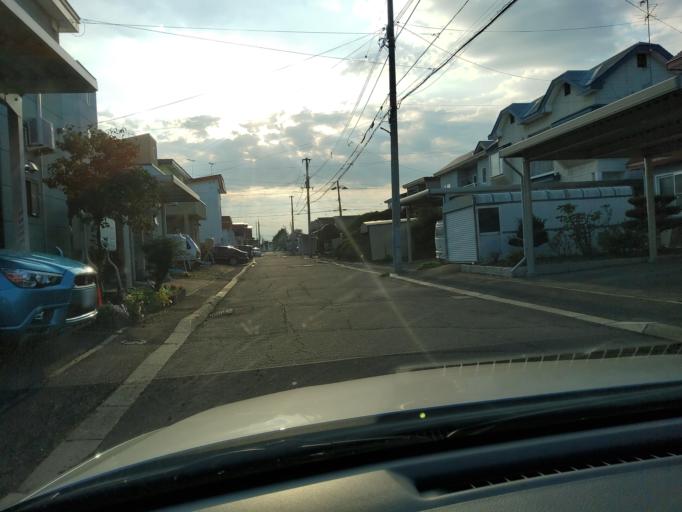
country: JP
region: Hokkaido
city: Obihiro
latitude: 42.9418
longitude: 143.1831
